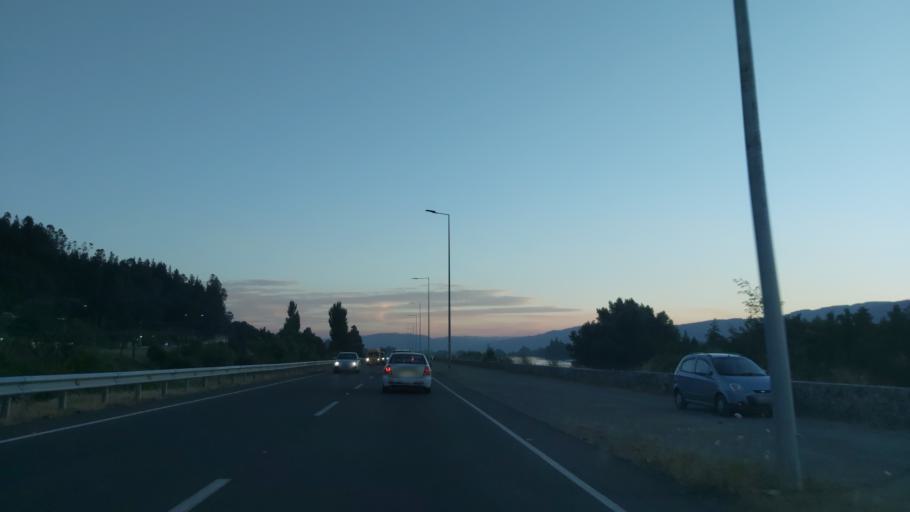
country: CL
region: Biobio
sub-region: Provincia de Concepcion
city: Chiguayante
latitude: -36.8828
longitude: -73.0387
